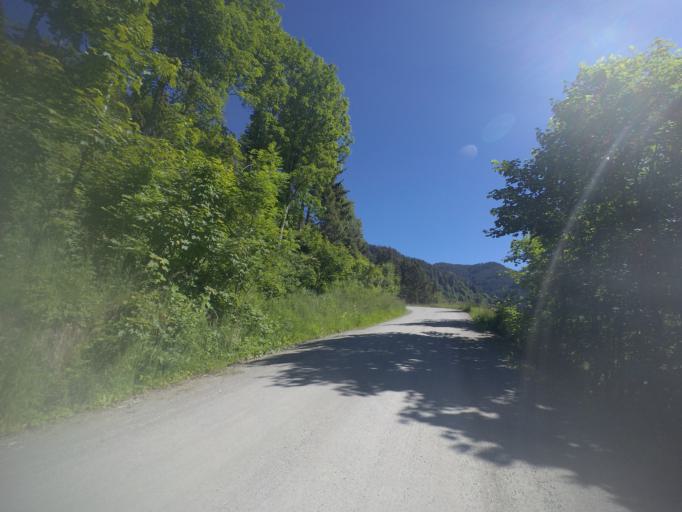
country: AT
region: Salzburg
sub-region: Politischer Bezirk Zell am See
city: Lend
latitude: 47.3273
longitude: 13.0657
